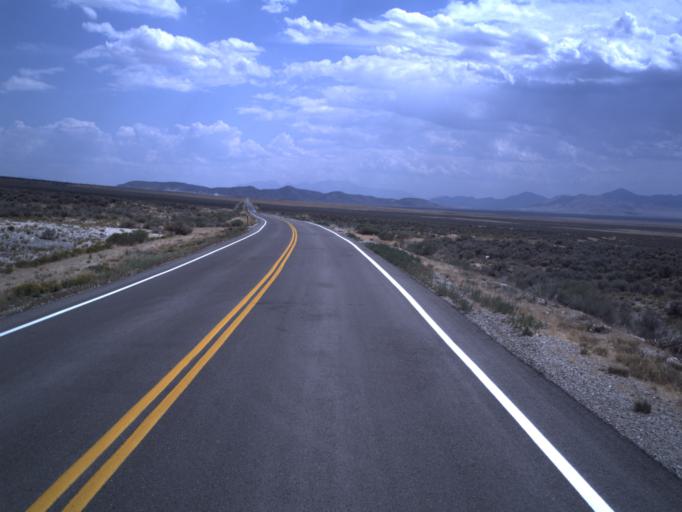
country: US
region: Utah
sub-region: Tooele County
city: Tooele
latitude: 40.2901
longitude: -112.2701
